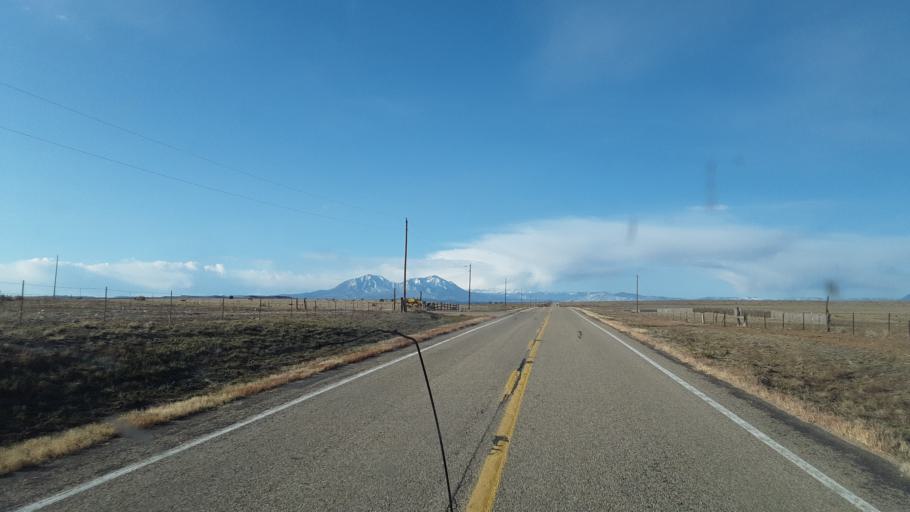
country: US
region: Colorado
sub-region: Huerfano County
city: Walsenburg
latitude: 37.6798
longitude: -104.6546
